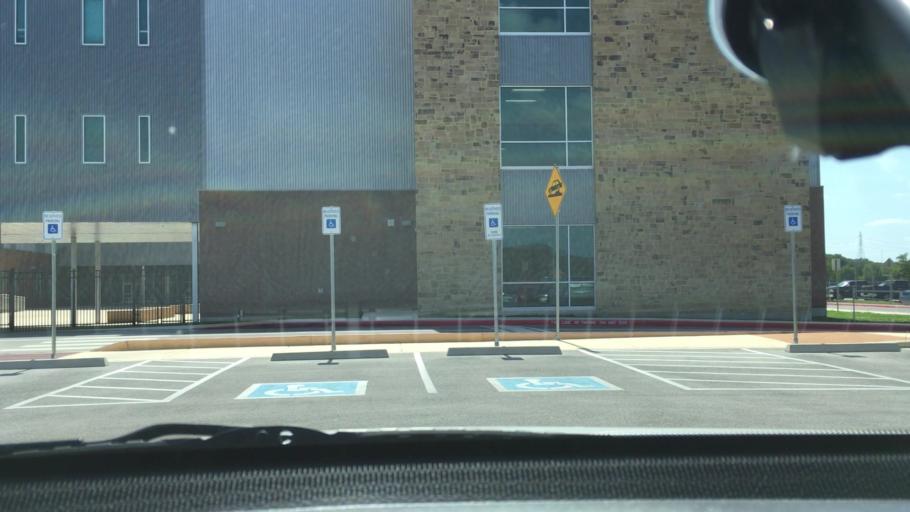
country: US
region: Texas
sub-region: Bexar County
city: Selma
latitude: 29.6098
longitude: -98.3362
